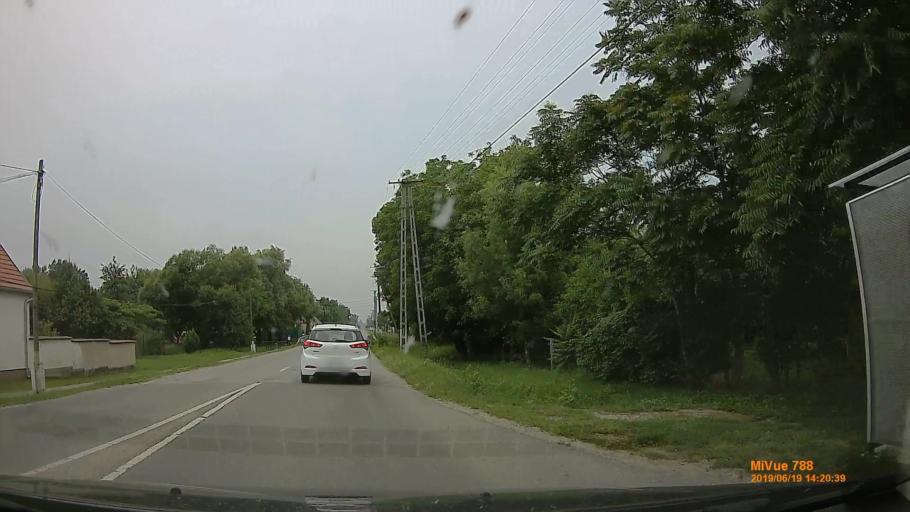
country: HU
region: Baranya
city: Szigetvar
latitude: 46.0238
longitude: 17.7769
